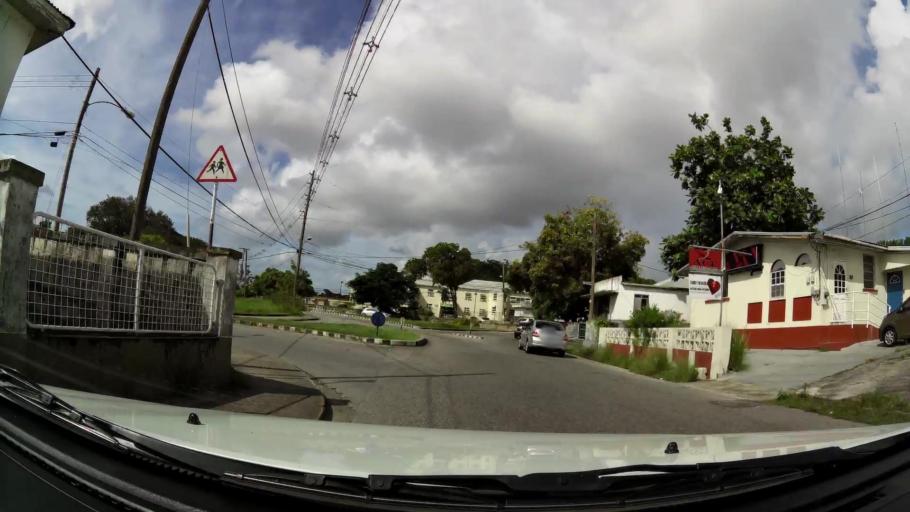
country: BB
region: Saint Michael
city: Bridgetown
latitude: 13.1047
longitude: -59.6017
